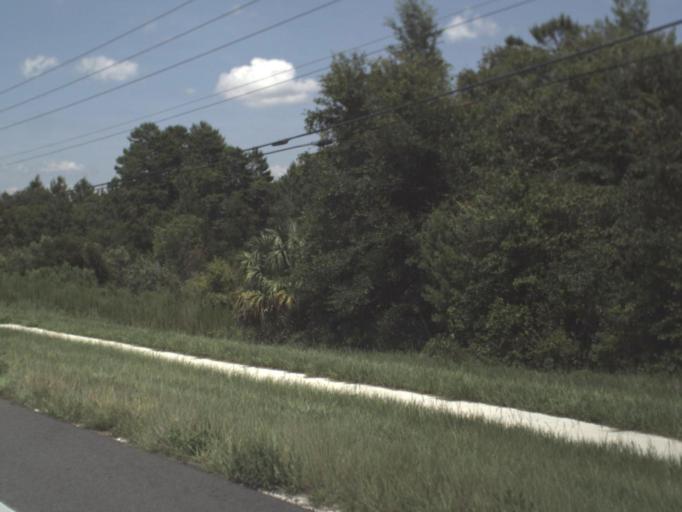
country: US
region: Florida
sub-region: Hernando County
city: North Weeki Wachee
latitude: 28.5343
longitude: -82.5670
